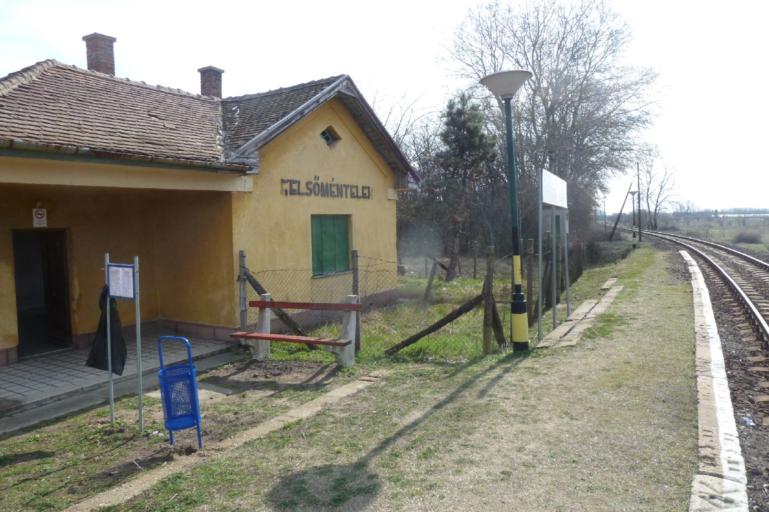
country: HU
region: Bacs-Kiskun
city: Lajosmizse
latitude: 46.9871
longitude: 19.5577
